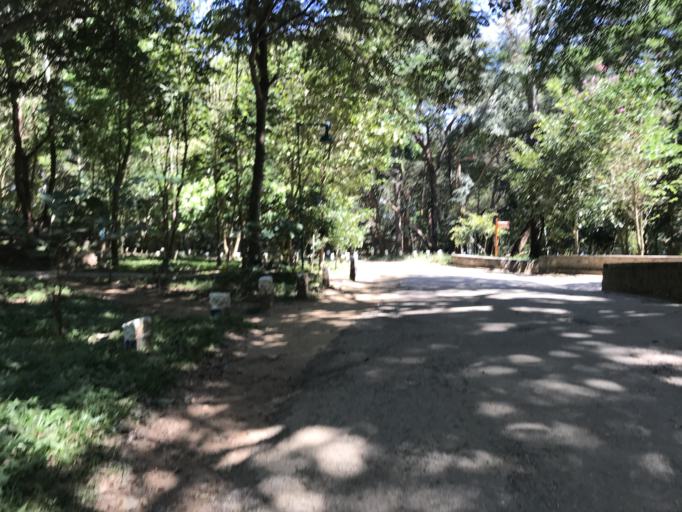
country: IN
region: Karnataka
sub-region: Mysore
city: Sargur
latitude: 11.9373
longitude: 76.2702
